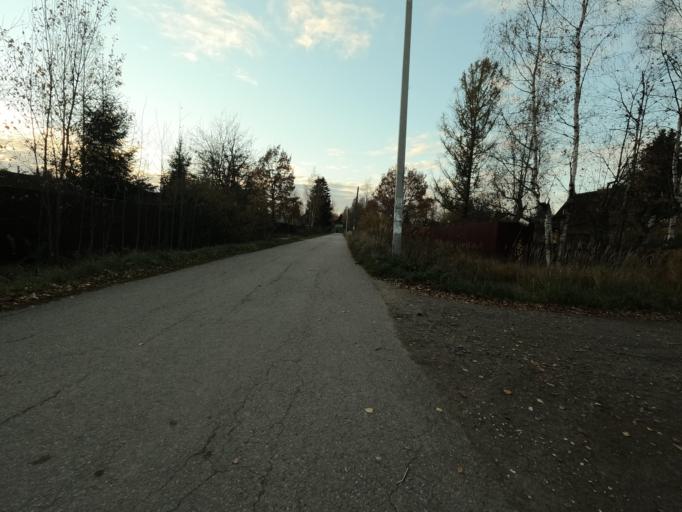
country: RU
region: Leningrad
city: Mga
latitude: 59.7764
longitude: 31.2088
